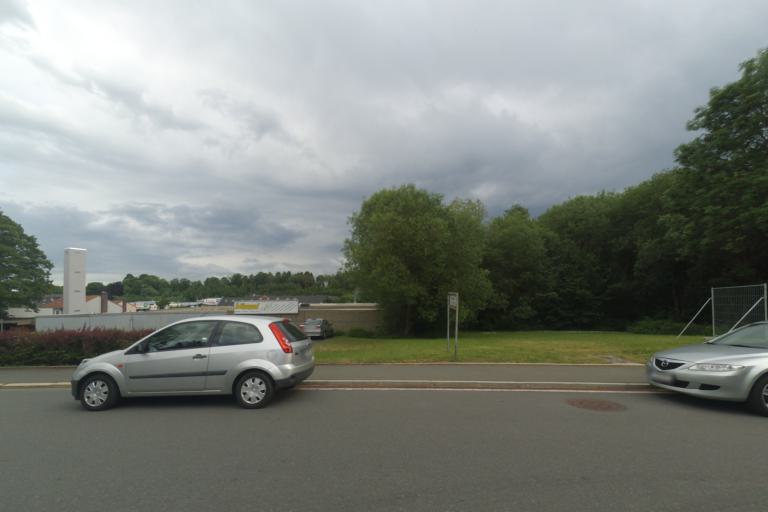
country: DE
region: Bavaria
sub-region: Upper Franconia
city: Munchberg
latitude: 50.1925
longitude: 11.7813
